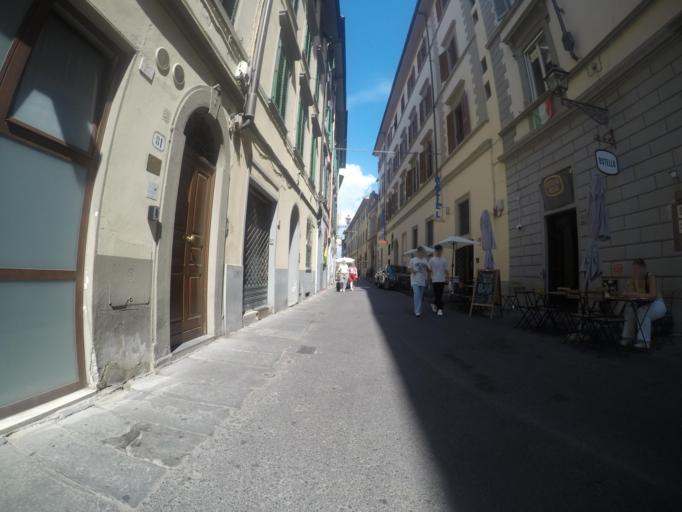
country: IT
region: Tuscany
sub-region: Province of Florence
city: Florence
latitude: 43.7779
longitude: 11.2509
